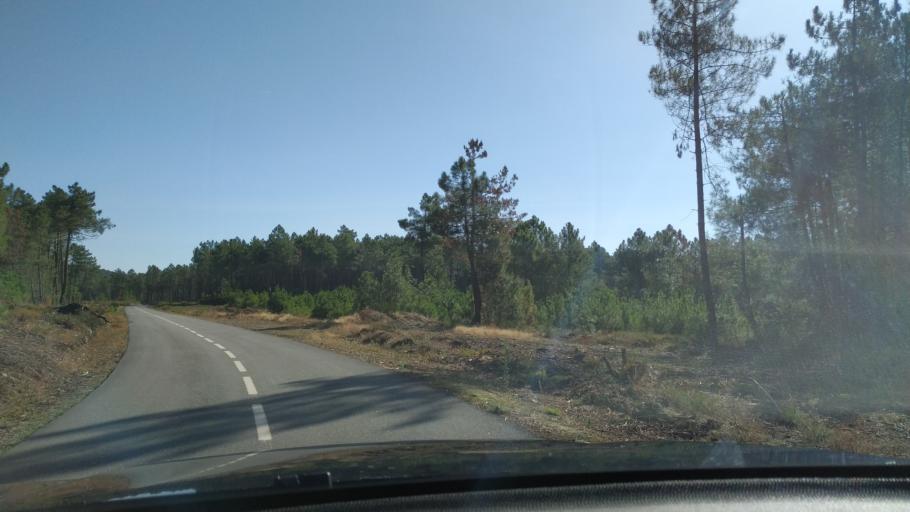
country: PT
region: Vila Real
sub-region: Sabrosa
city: Vilela
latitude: 41.2277
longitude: -7.6152
